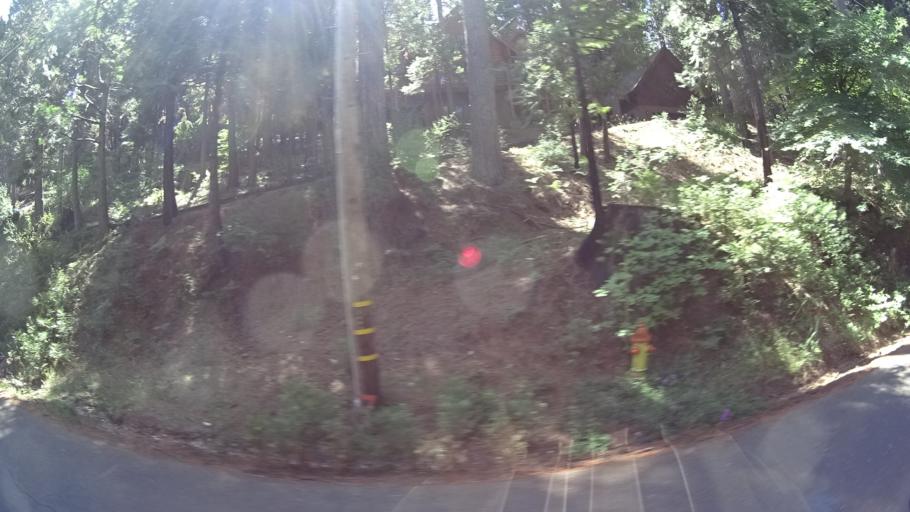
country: US
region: California
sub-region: Calaveras County
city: Arnold
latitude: 38.2411
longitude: -120.3745
